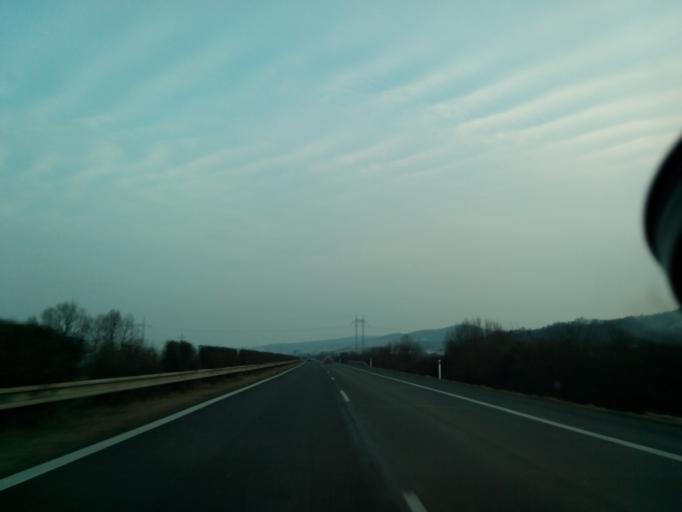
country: SK
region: Presovsky
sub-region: Okres Presov
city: Presov
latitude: 48.8896
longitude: 21.2489
